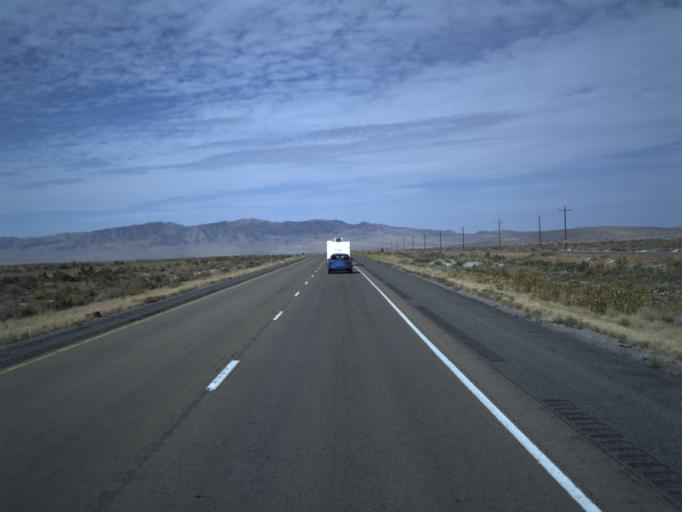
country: US
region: Utah
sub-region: Tooele County
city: Grantsville
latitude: 40.7489
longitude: -112.6808
